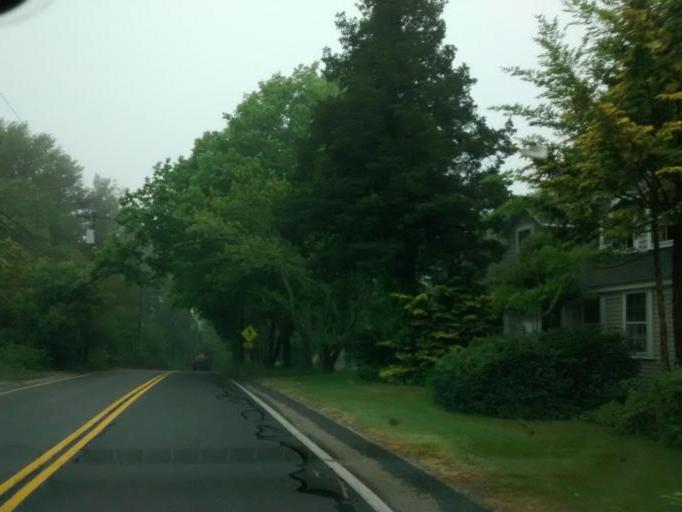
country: US
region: Massachusetts
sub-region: Barnstable County
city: Monument Beach
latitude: 41.7163
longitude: -70.6091
